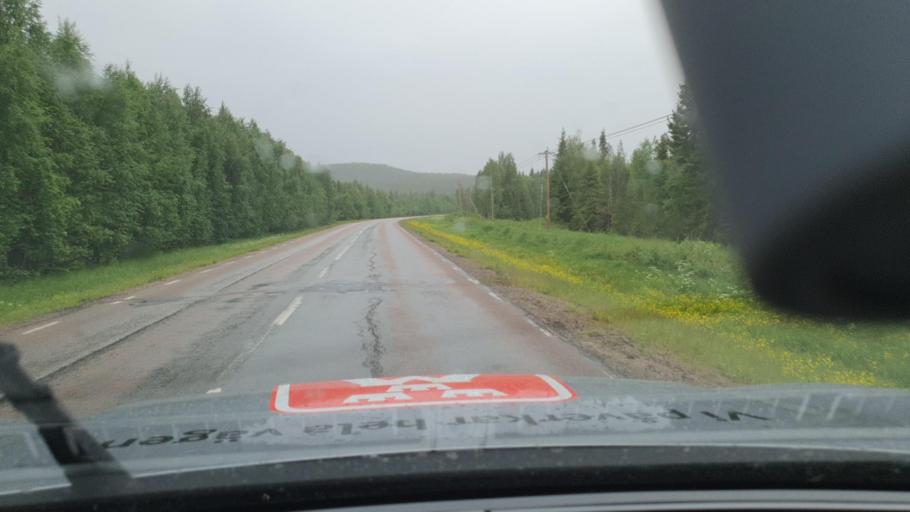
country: SE
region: Norrbotten
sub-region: Overtornea Kommun
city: OEvertornea
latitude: 66.4491
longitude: 23.2722
